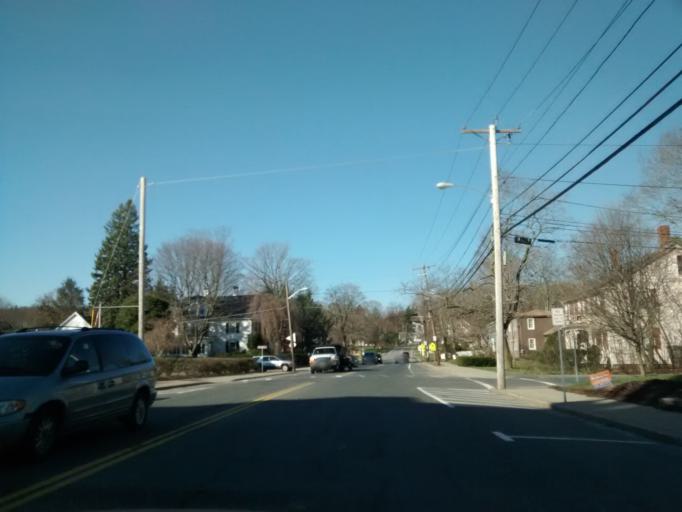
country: US
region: Massachusetts
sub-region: Worcester County
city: Westborough
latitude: 42.2666
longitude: -71.6164
